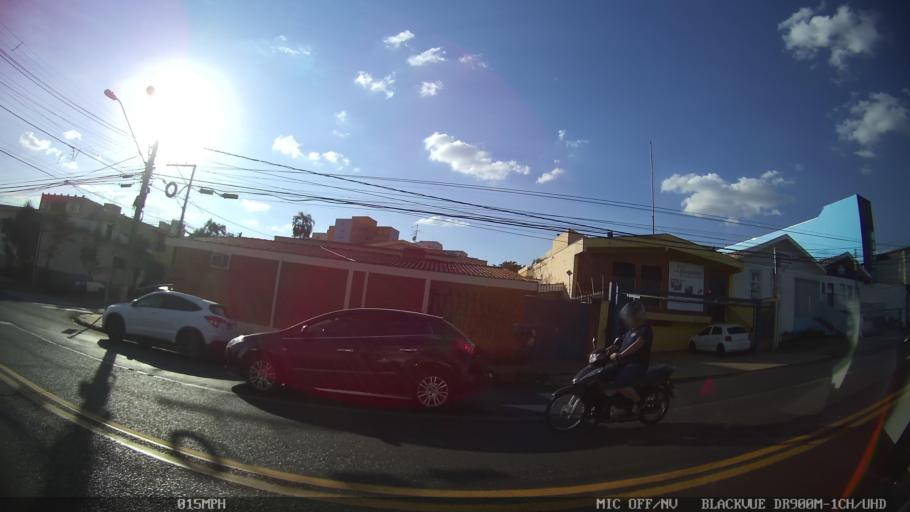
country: BR
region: Sao Paulo
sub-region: Ribeirao Preto
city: Ribeirao Preto
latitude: -21.1876
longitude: -47.7925
